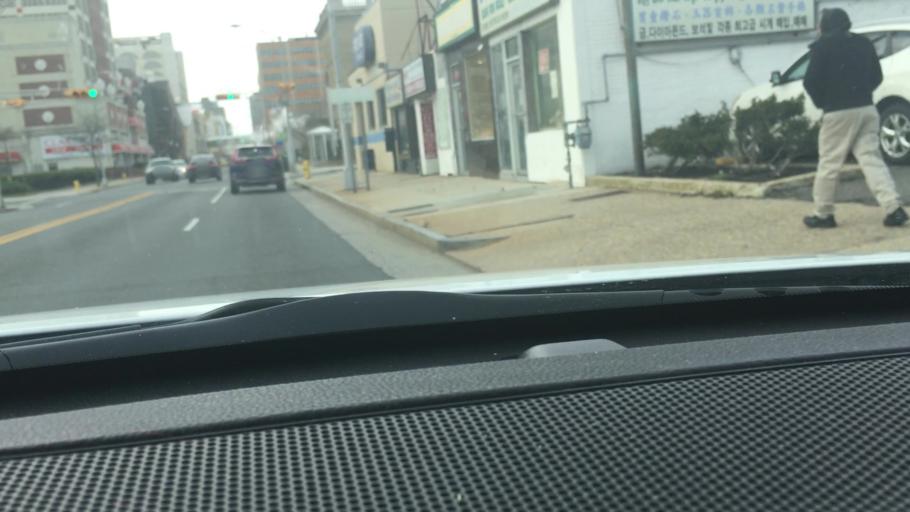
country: US
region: New Jersey
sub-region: Atlantic County
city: Atlantic City
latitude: 39.3588
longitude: -74.4316
